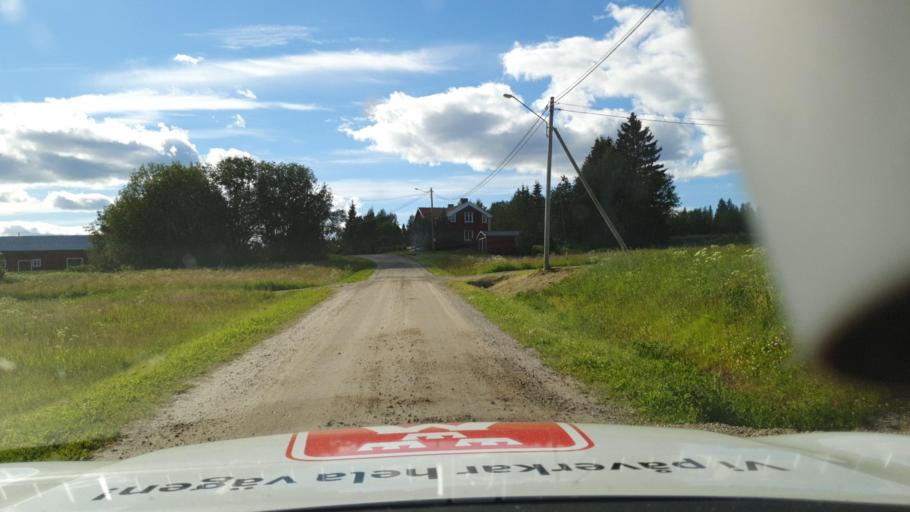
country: SE
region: Vaesterbotten
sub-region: Lycksele Kommun
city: Lycksele
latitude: 64.4010
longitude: 18.4042
